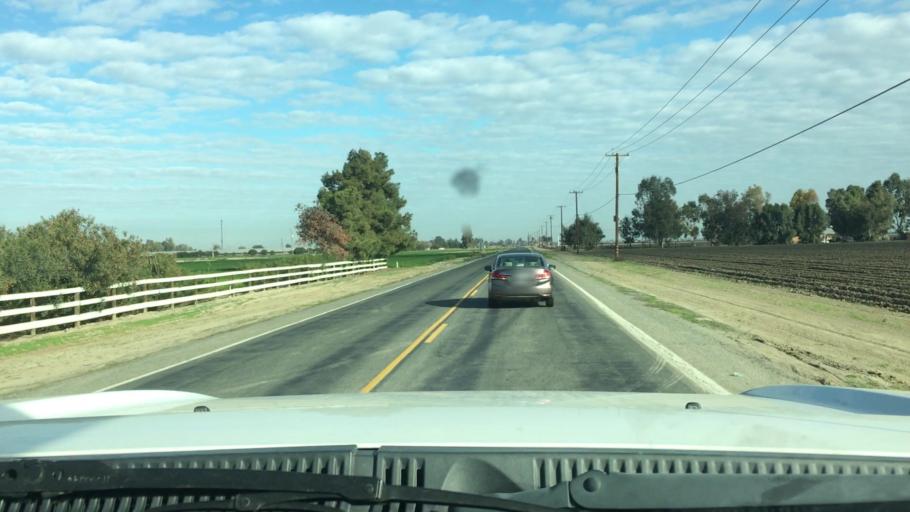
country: US
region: California
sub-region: Kings County
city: Stratford
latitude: 36.2123
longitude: -119.7802
